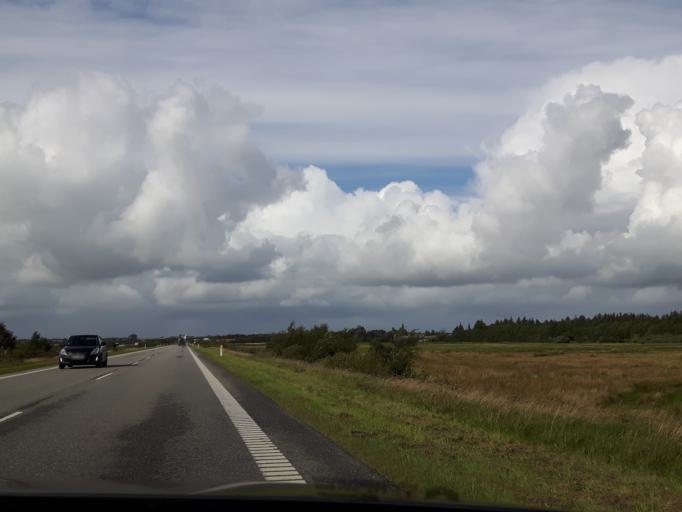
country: DK
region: North Denmark
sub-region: Vesthimmerland Kommune
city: Logstor
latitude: 57.0232
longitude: 9.0321
